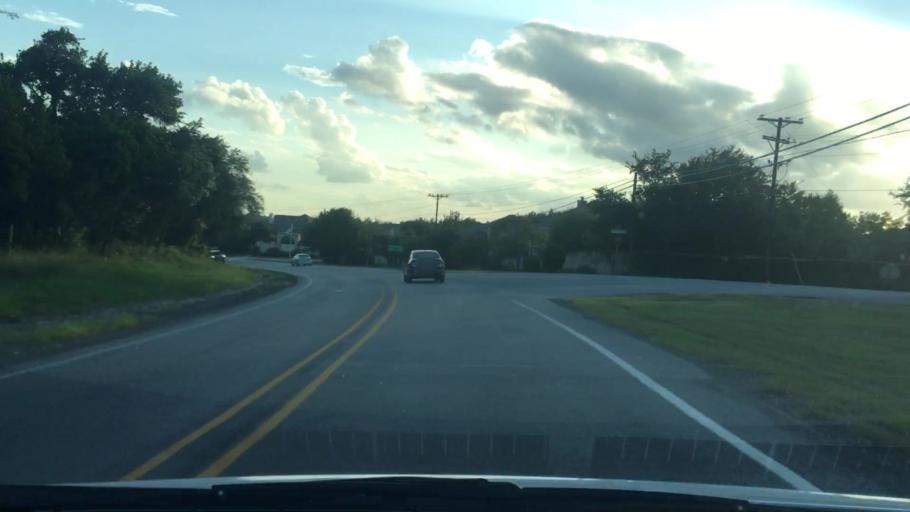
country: US
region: Texas
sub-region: Williamson County
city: Anderson Mill
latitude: 30.4577
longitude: -97.8455
